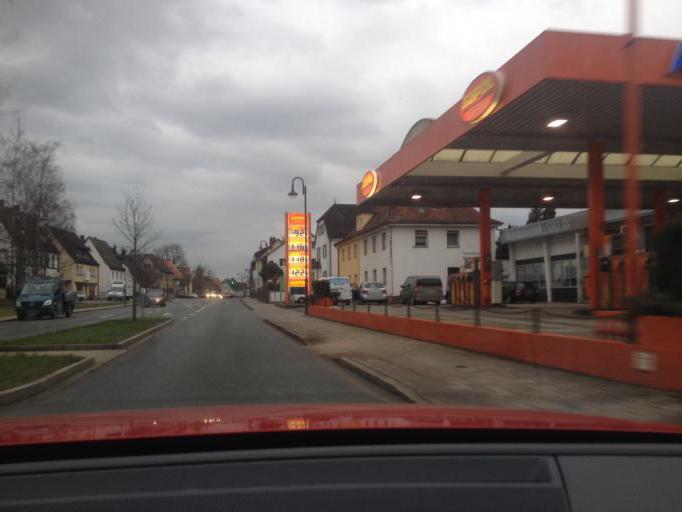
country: DE
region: Bavaria
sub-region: Regierungsbezirk Mittelfranken
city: Ruckersdorf
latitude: 49.4957
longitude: 11.2462
